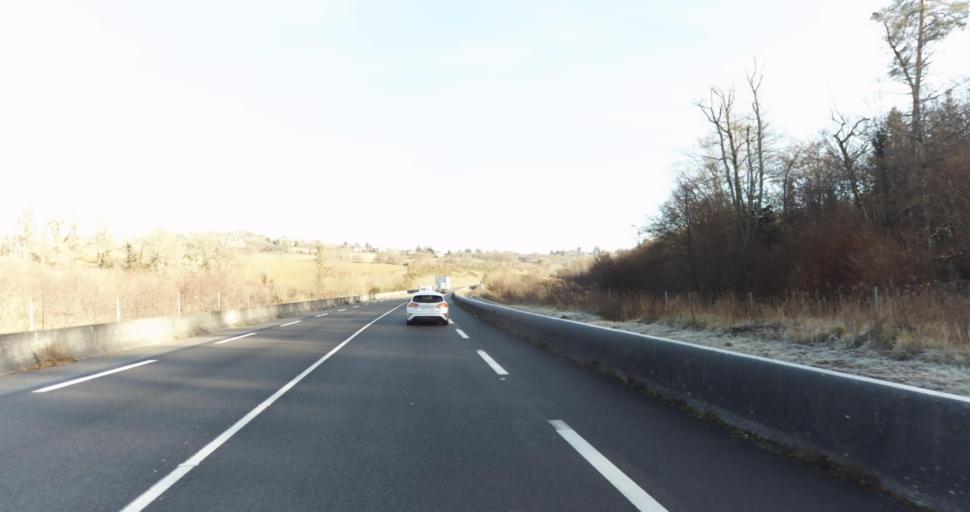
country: FR
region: Limousin
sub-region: Departement de la Haute-Vienne
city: Aixe-sur-Vienne
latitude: 45.8263
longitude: 1.1337
